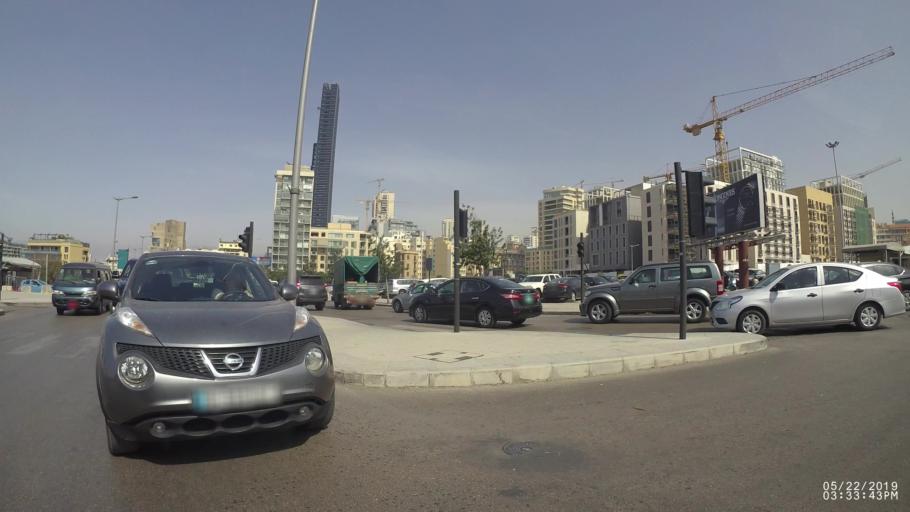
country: LB
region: Beyrouth
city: Beirut
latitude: 33.8975
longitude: 35.5078
